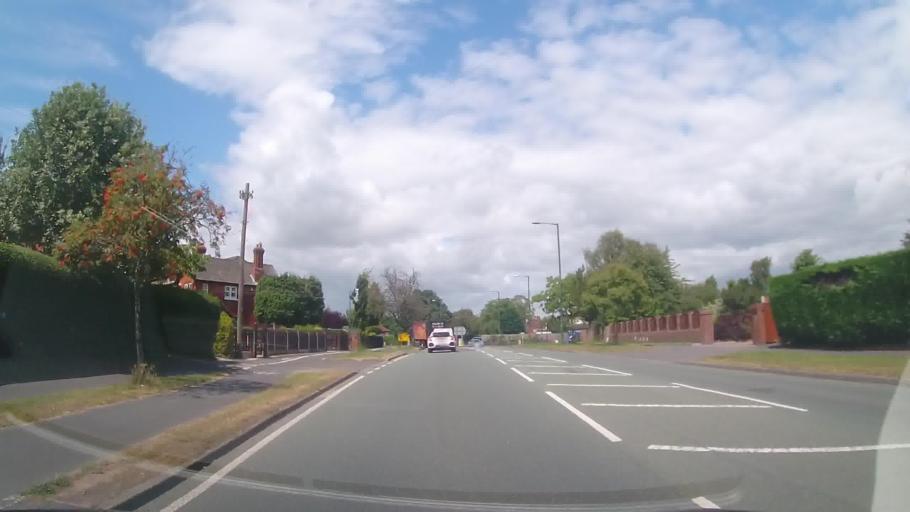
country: GB
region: England
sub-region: Shropshire
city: Shrewsbury
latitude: 52.7047
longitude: -2.7727
